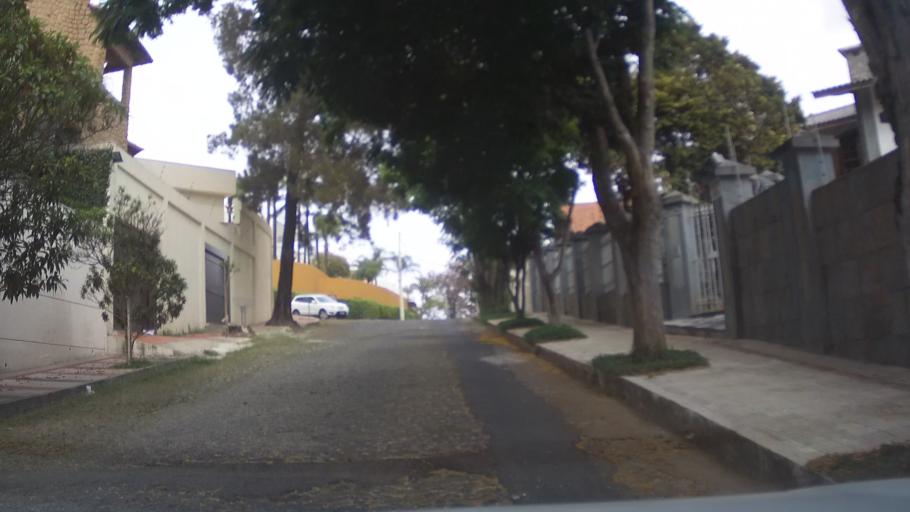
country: BR
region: Minas Gerais
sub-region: Belo Horizonte
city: Belo Horizonte
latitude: -19.9550
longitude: -43.9229
